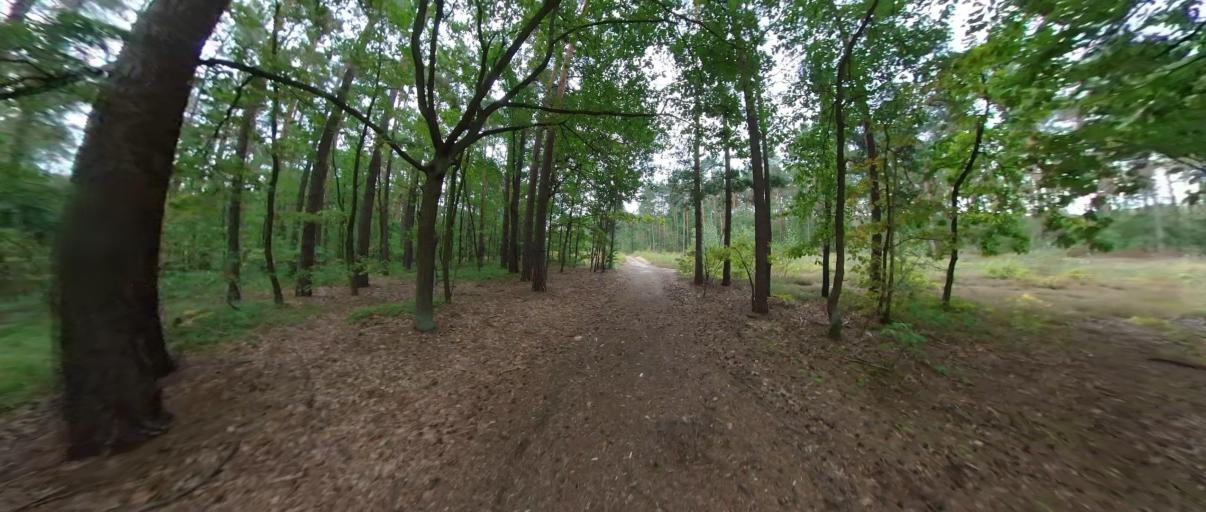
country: PL
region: Masovian Voivodeship
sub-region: Powiat bialobrzeski
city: Bialobrzegi
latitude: 51.6463
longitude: 20.9697
